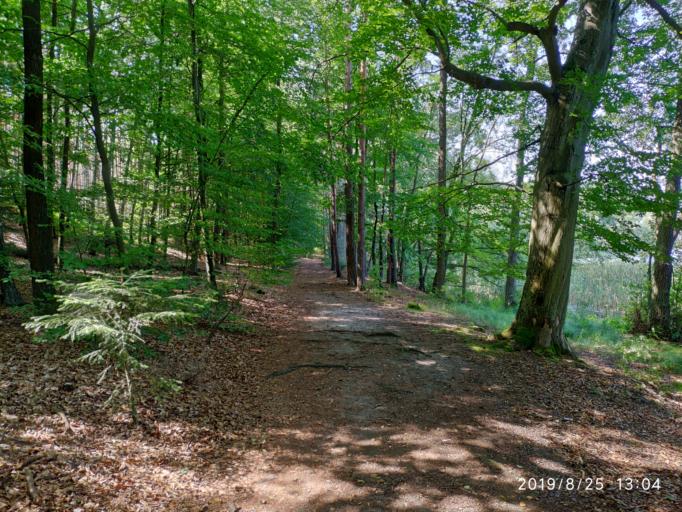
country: PL
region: Lubusz
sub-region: Powiat krosnienski
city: Dabie
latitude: 51.9925
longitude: 15.1612
